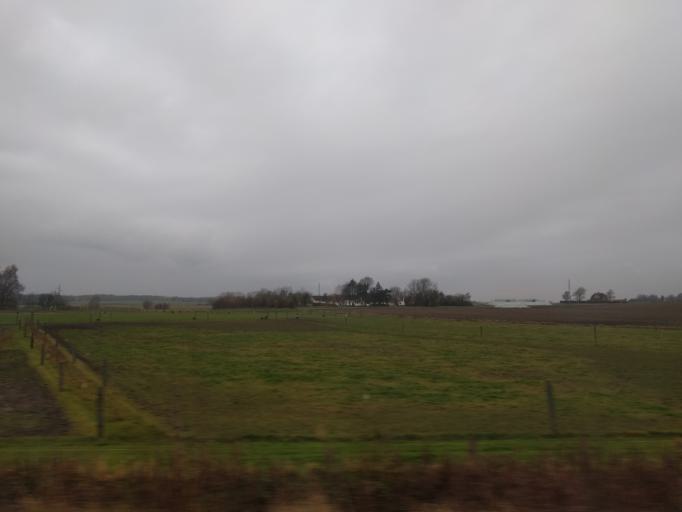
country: DK
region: Zealand
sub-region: Slagelse Kommune
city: Forlev
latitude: 55.3769
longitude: 11.2624
